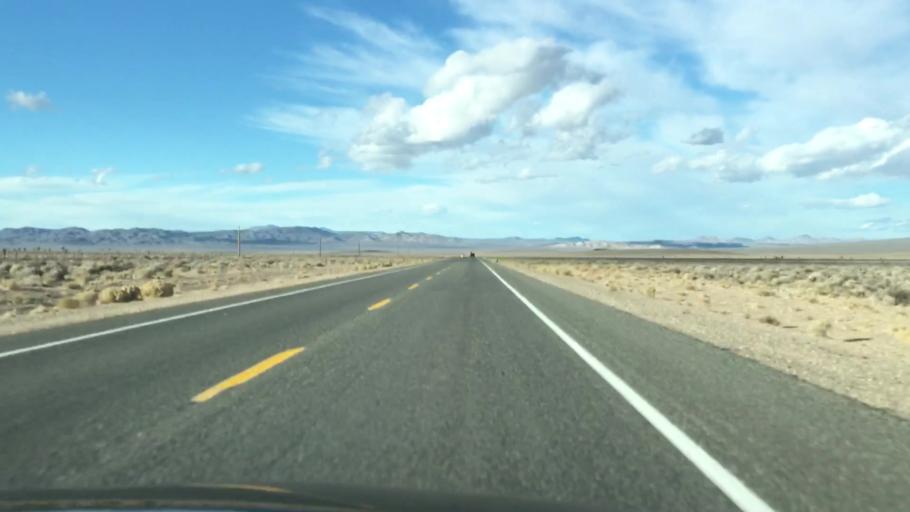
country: US
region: Nevada
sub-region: Esmeralda County
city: Goldfield
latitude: 37.3962
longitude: -117.1470
